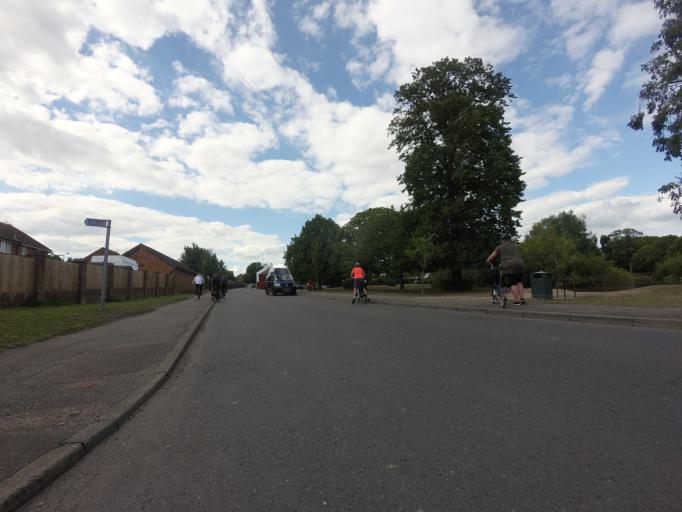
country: GB
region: England
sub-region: East Sussex
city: Hailsham
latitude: 50.8587
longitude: 0.2580
